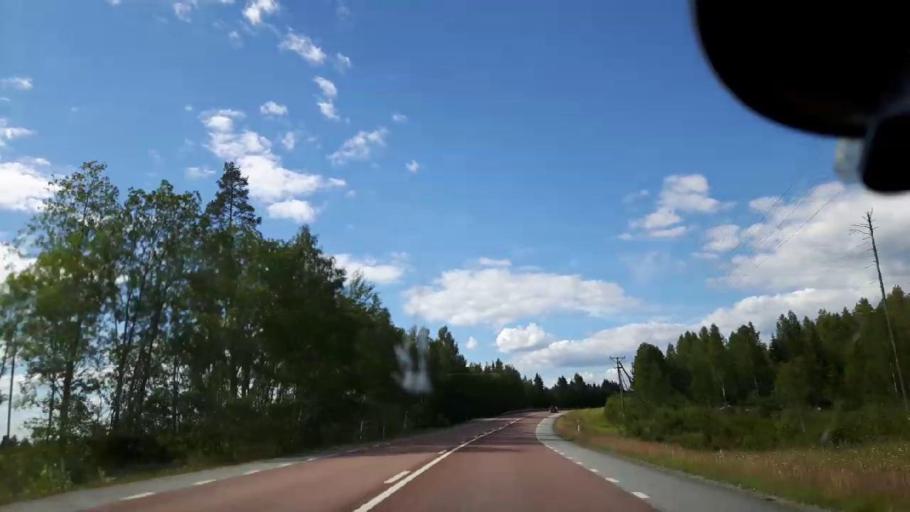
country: SE
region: Jaemtland
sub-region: Braecke Kommun
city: Braecke
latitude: 62.7784
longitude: 15.3885
